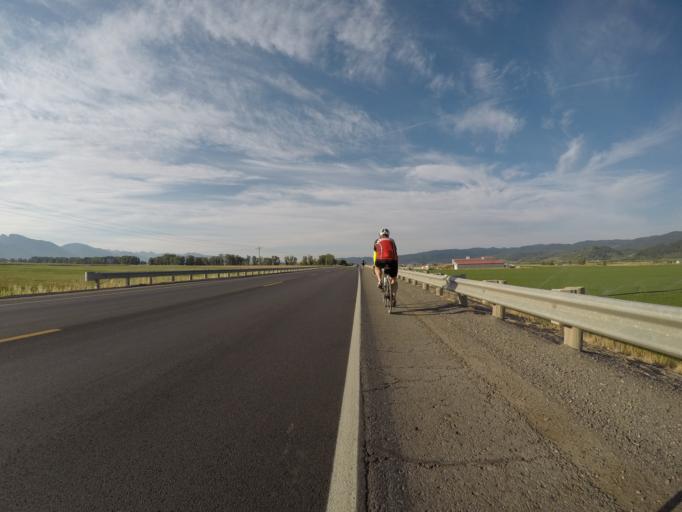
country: US
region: Wyoming
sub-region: Lincoln County
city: Afton
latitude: 42.9746
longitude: -111.0125
